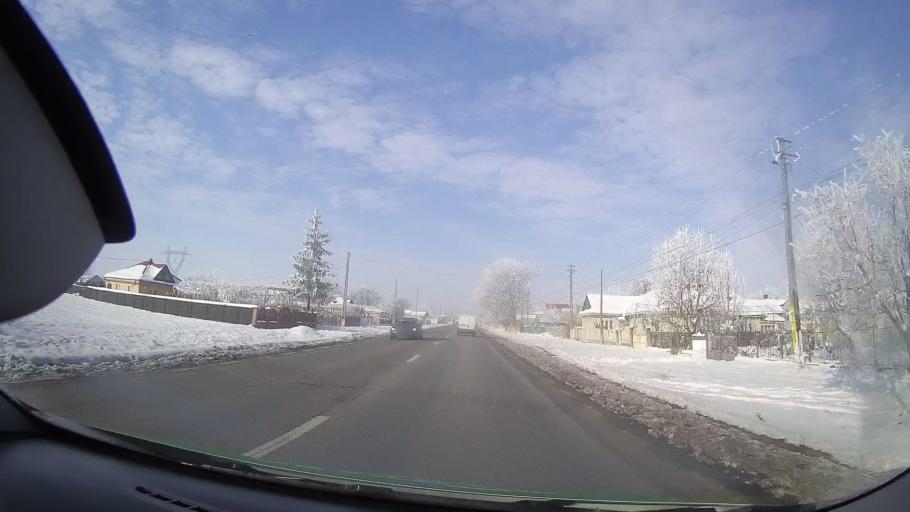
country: RO
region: Iasi
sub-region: Comuna Cristesti
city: Cristesti
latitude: 47.2474
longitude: 26.5719
